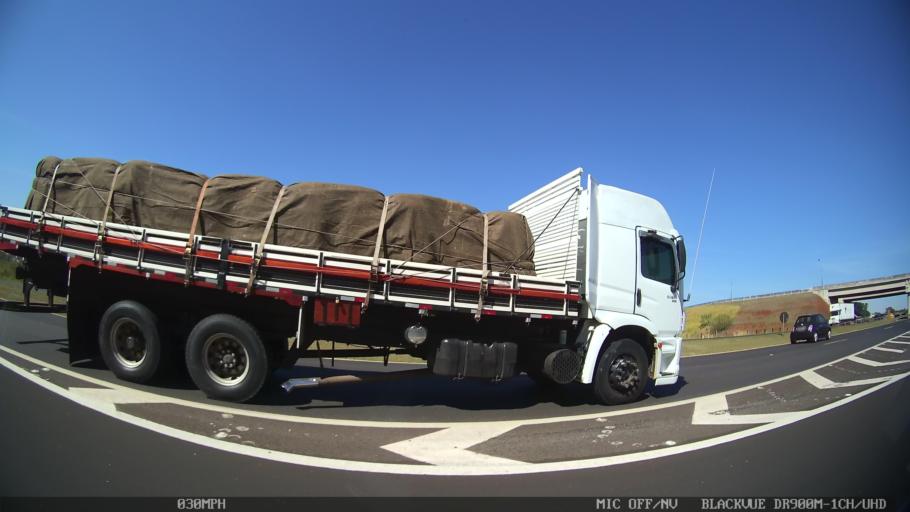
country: BR
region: Sao Paulo
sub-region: Ribeirao Preto
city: Ribeirao Preto
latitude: -21.2217
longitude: -47.7761
